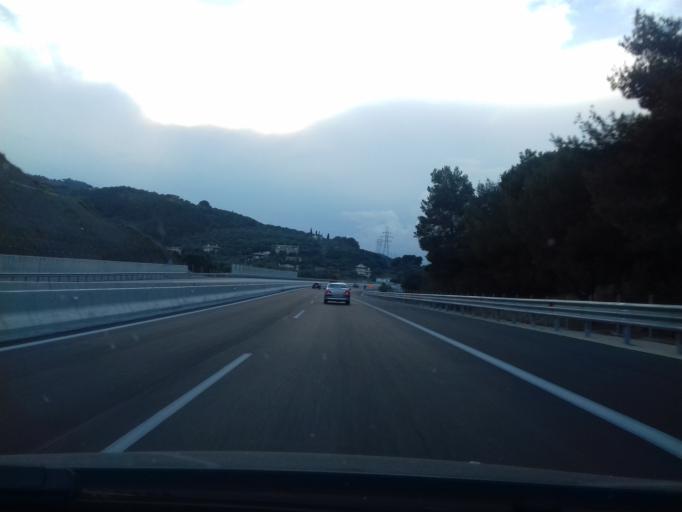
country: GR
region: West Greece
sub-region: Nomos Achaias
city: Kamarai
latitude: 38.3068
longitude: 21.9923
